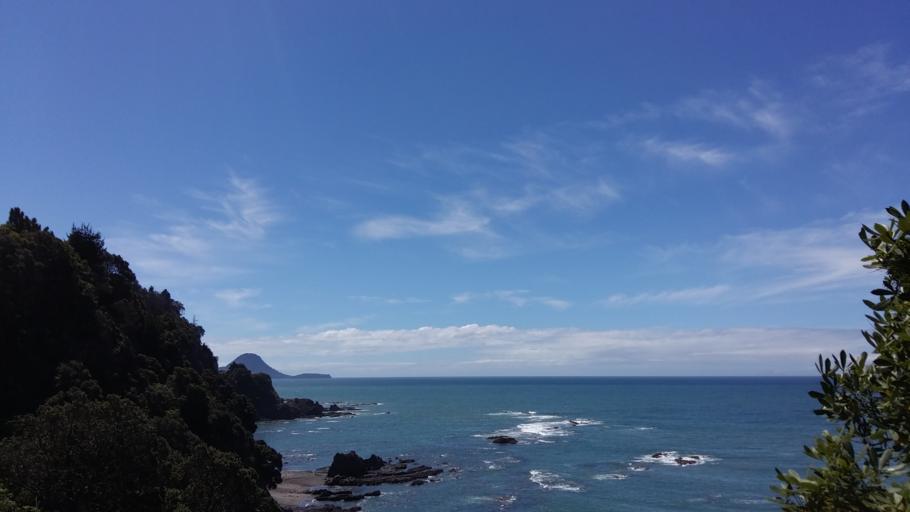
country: NZ
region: Bay of Plenty
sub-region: Whakatane District
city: Whakatane
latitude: -37.9464
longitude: 177.0213
